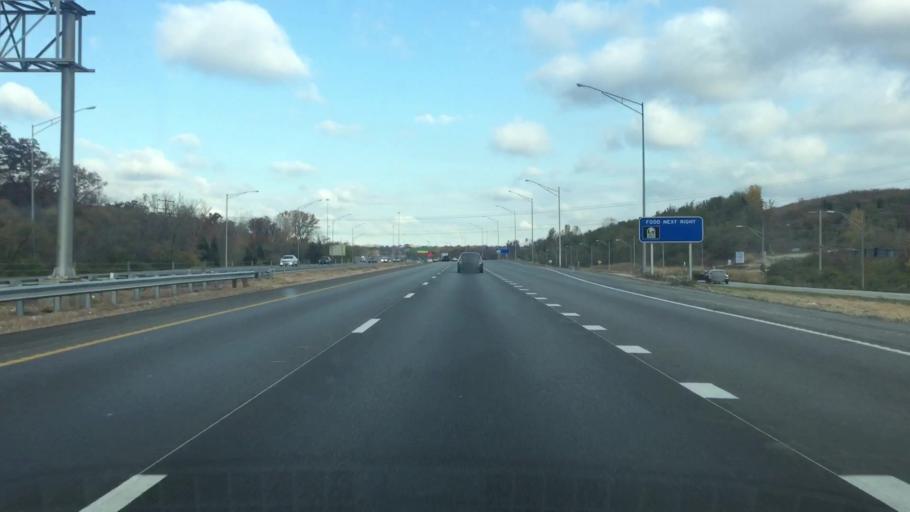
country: US
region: Kansas
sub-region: Johnson County
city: Leawood
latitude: 38.9619
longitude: -94.5421
